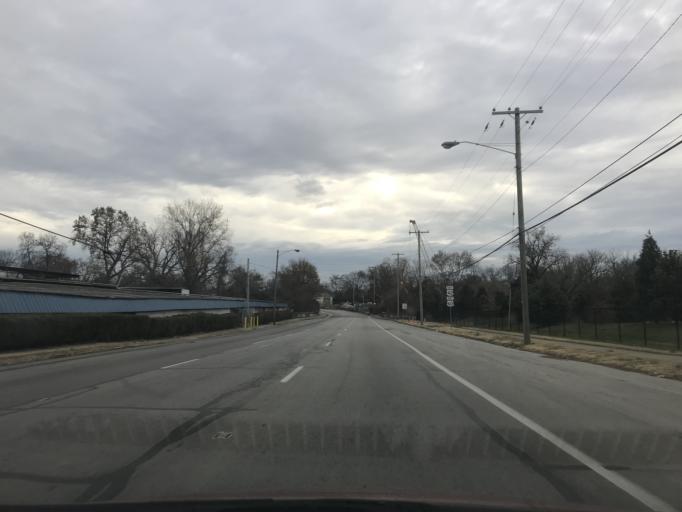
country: US
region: Indiana
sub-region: Clark County
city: Jeffersonville
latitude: 38.2536
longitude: -85.7291
